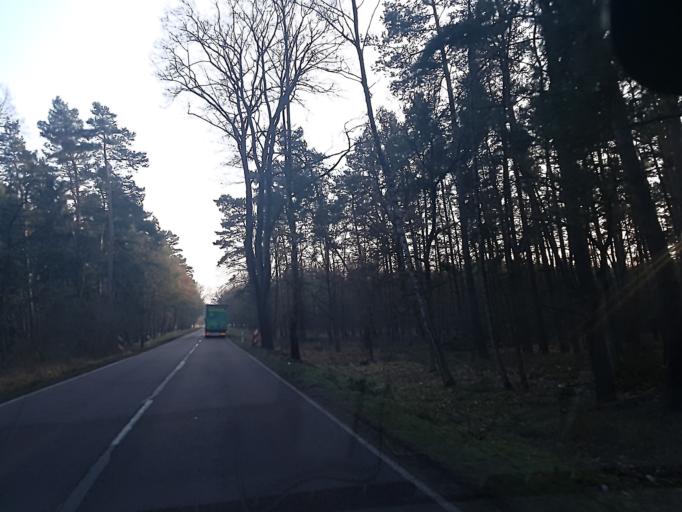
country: DE
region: Saxony-Anhalt
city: Coswig
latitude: 51.9693
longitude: 12.4657
